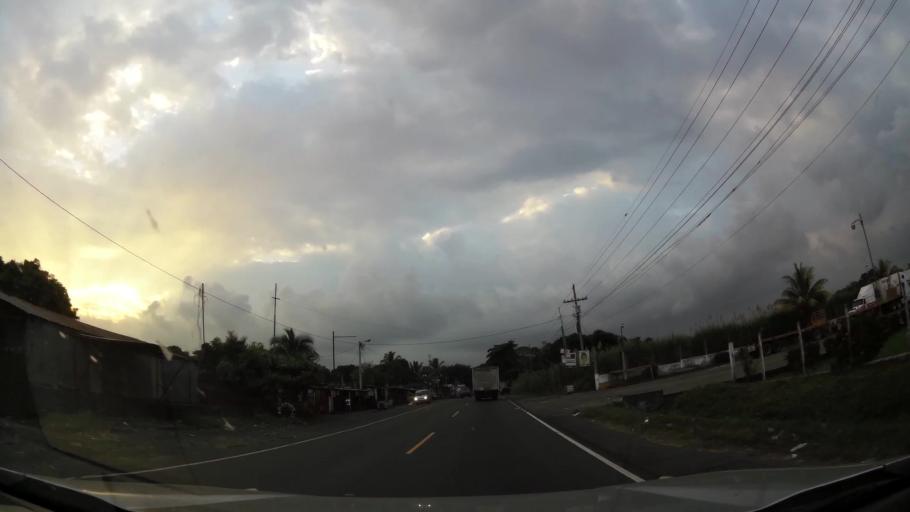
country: GT
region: Escuintla
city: Siquinala
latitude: 14.3036
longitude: -90.9598
